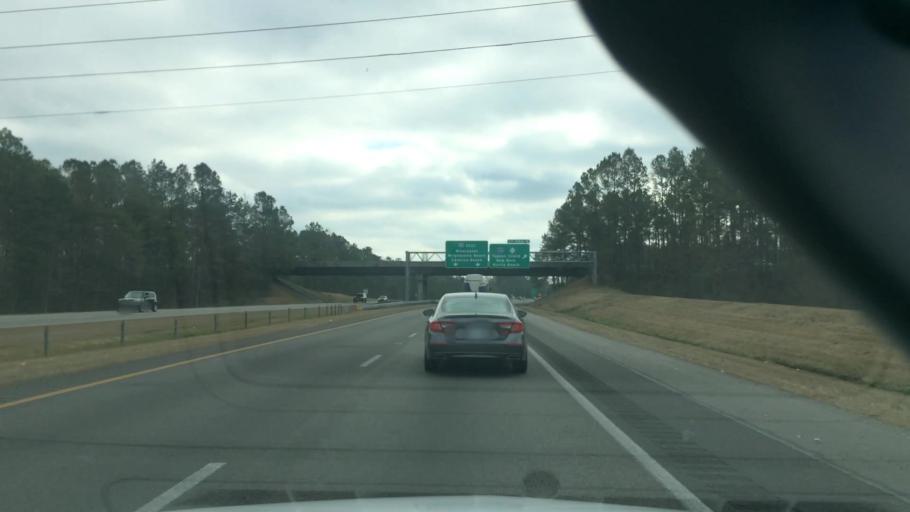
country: US
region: North Carolina
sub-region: New Hanover County
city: Skippers Corner
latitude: 34.3288
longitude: -77.8739
